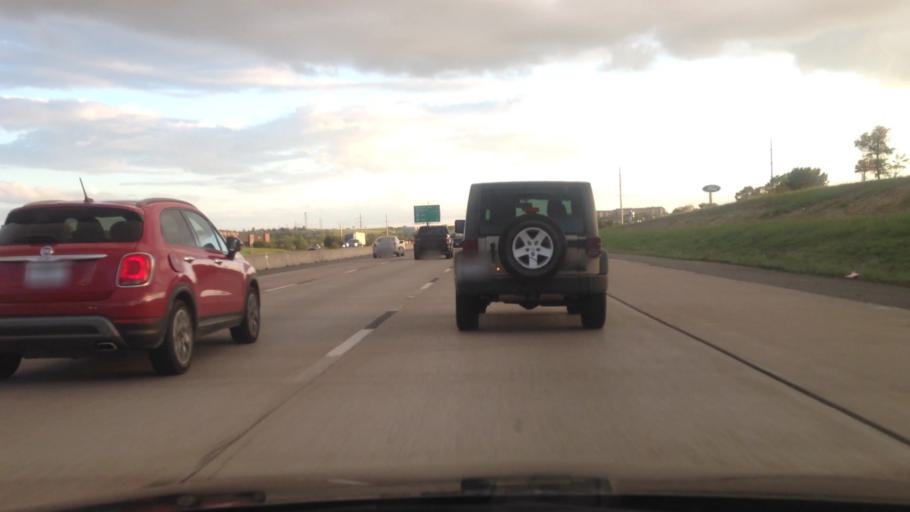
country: US
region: Texas
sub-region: Tarrant County
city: White Settlement
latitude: 32.7603
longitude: -97.4780
